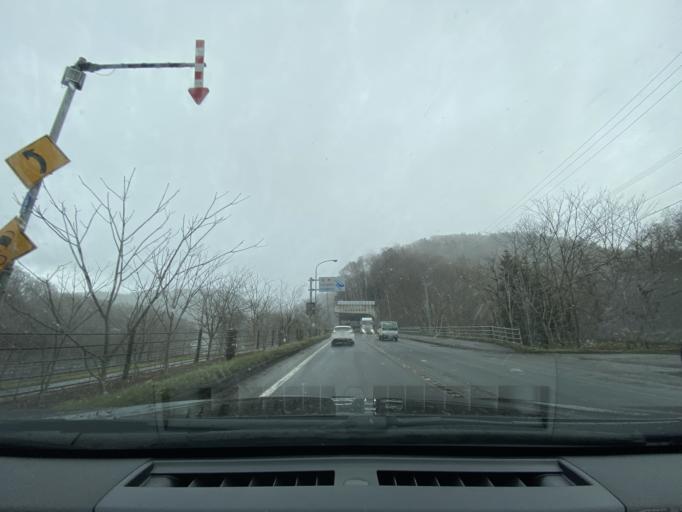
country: JP
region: Hokkaido
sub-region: Asahikawa-shi
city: Asahikawa
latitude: 43.7358
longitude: 142.2379
